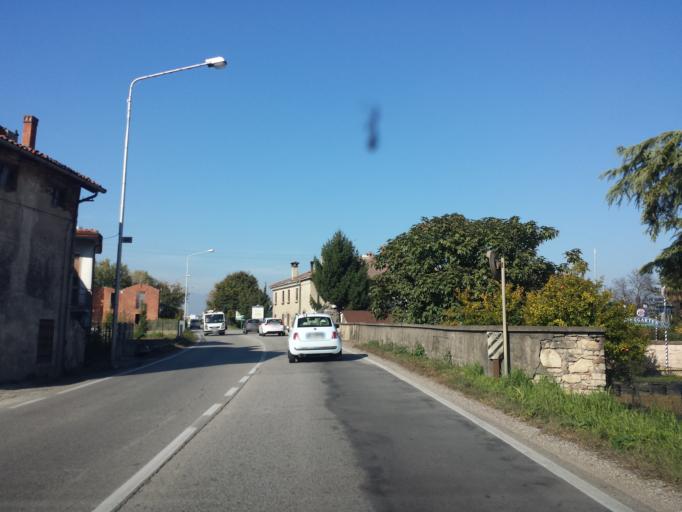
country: IT
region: Veneto
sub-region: Provincia di Vicenza
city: Crispi Cavour
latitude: 45.5786
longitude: 11.5090
